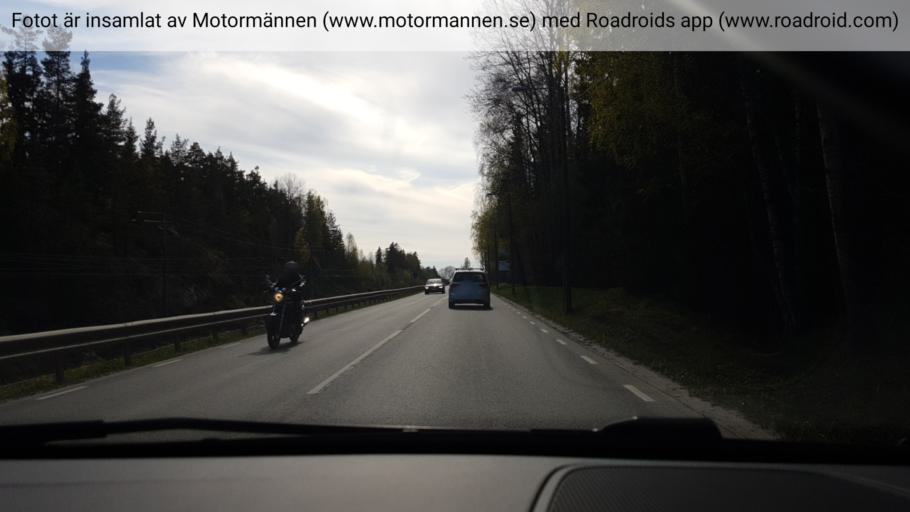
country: SE
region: Stockholm
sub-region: Botkyrka Kommun
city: Tullinge
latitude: 59.2112
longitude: 17.9260
